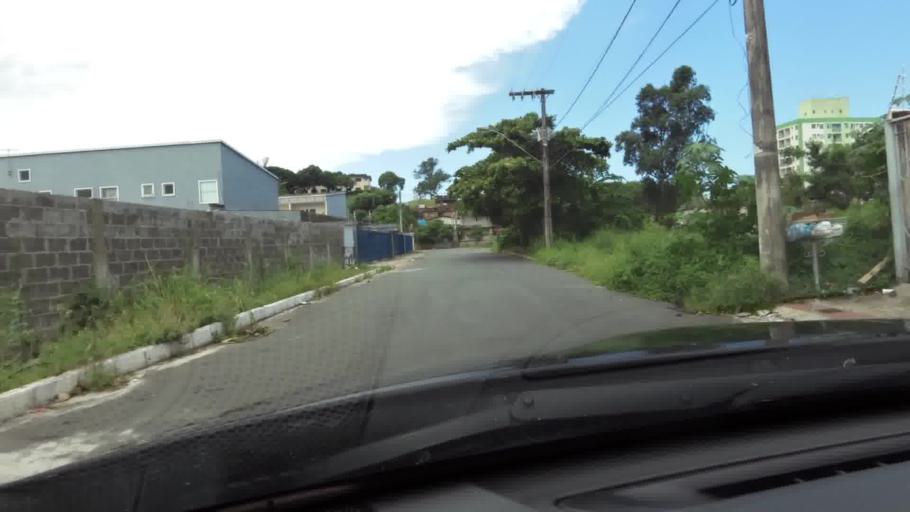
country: BR
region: Espirito Santo
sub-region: Guarapari
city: Guarapari
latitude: -20.6421
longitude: -40.4824
